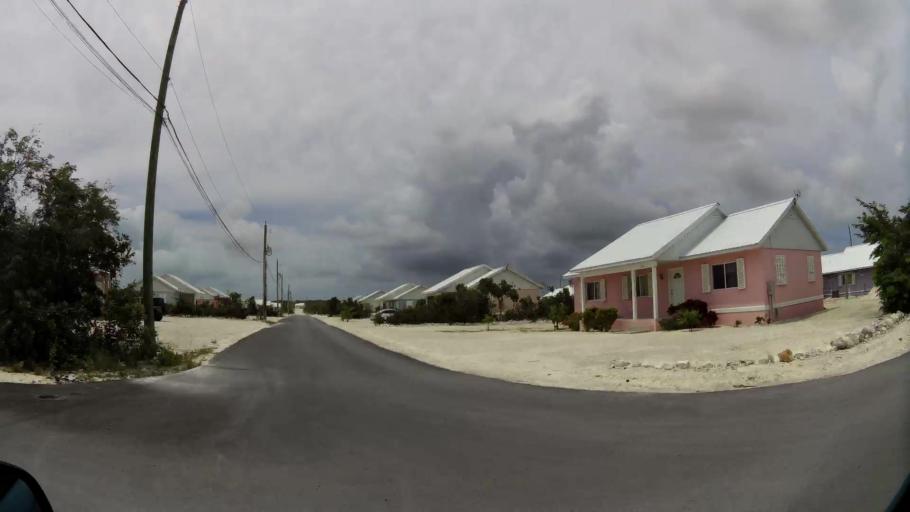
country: BS
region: Mayaguana
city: Abraham's Bay
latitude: 21.8068
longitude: -72.2929
